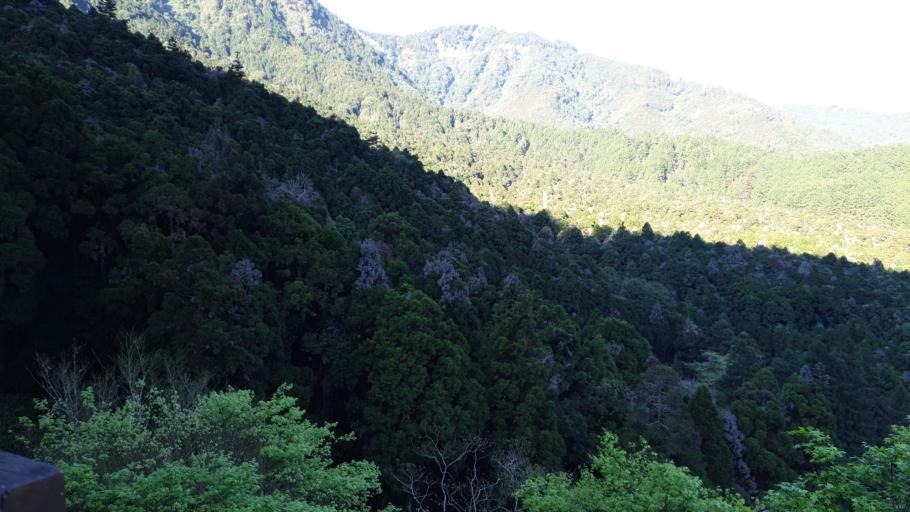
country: TW
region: Taiwan
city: Lugu
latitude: 23.6656
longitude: 120.7992
